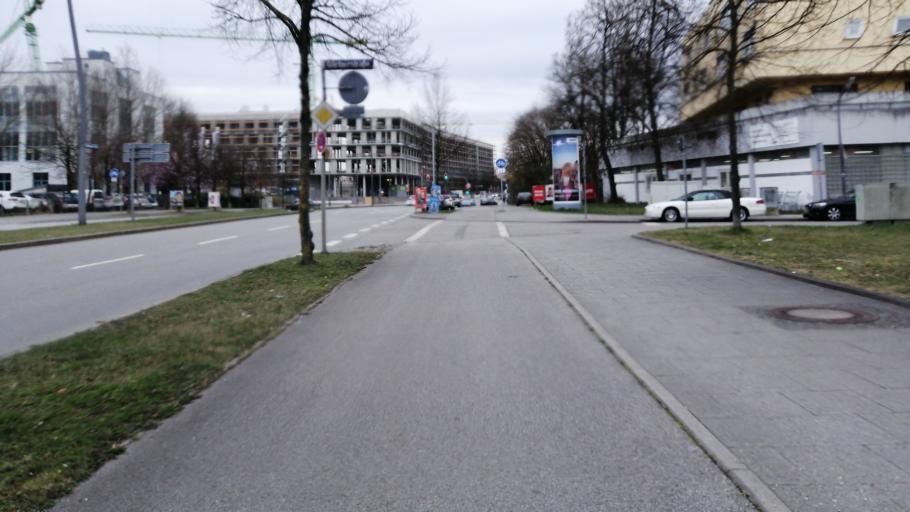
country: DE
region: Bavaria
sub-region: Upper Bavaria
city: Munich
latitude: 48.1779
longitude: 11.5288
